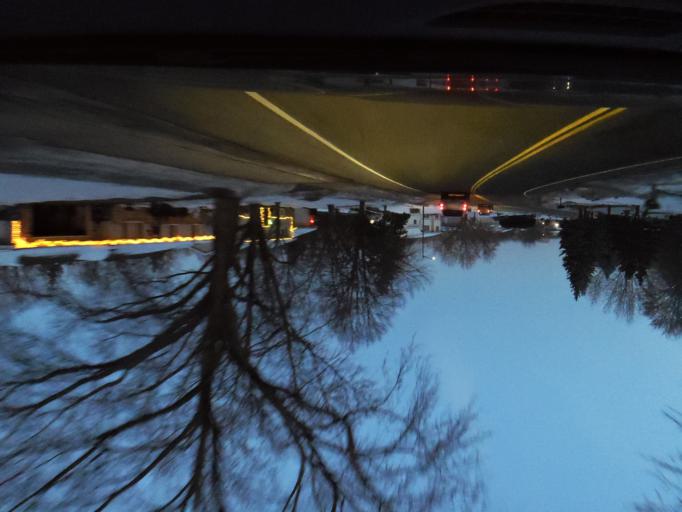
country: US
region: Minnesota
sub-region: Scott County
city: Prior Lake
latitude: 44.7119
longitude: -93.4147
